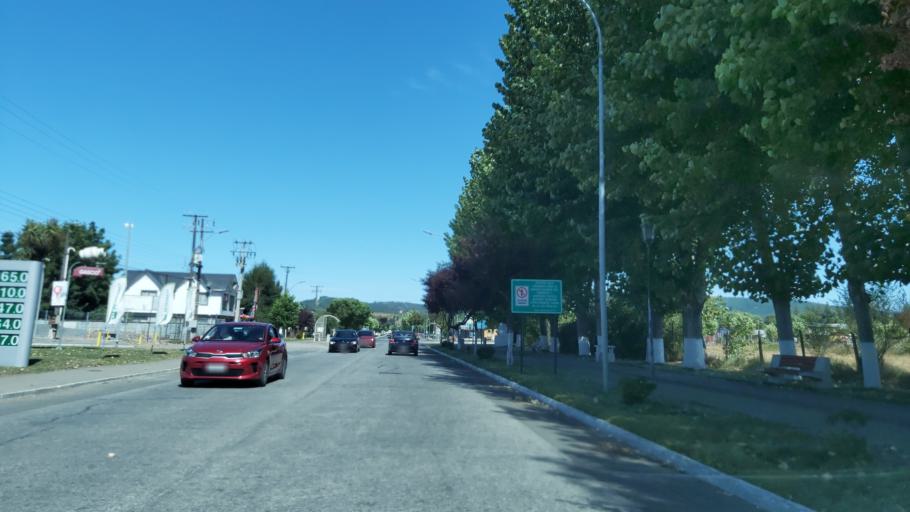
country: CL
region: Biobio
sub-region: Provincia de Concepcion
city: Lota
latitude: -37.1677
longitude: -72.9504
